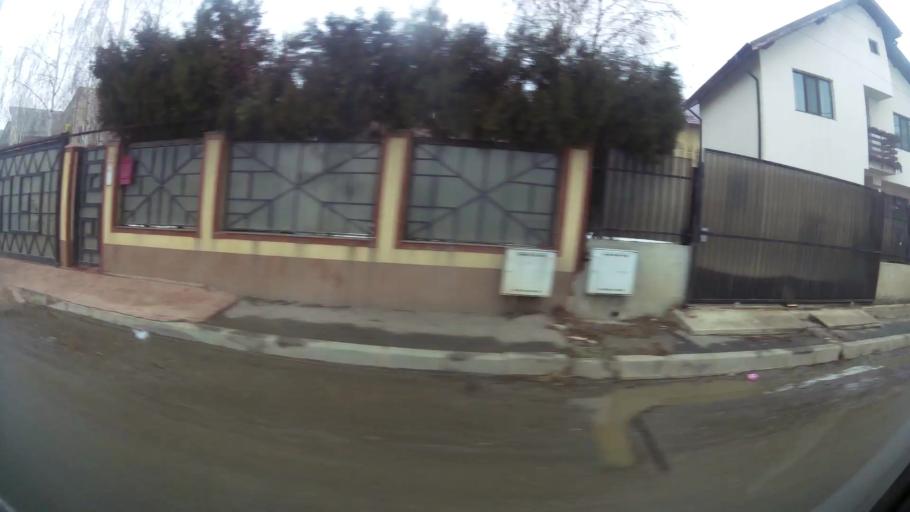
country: RO
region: Ilfov
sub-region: Comuna Chiajna
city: Chiajna
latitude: 44.4520
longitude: 25.9860
